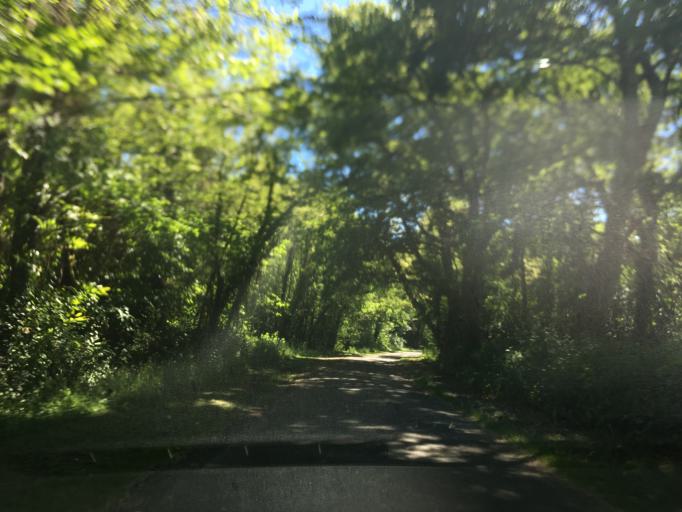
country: FR
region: Aquitaine
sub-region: Departement de la Gironde
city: Lesparre-Medoc
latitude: 45.2916
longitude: -0.8944
